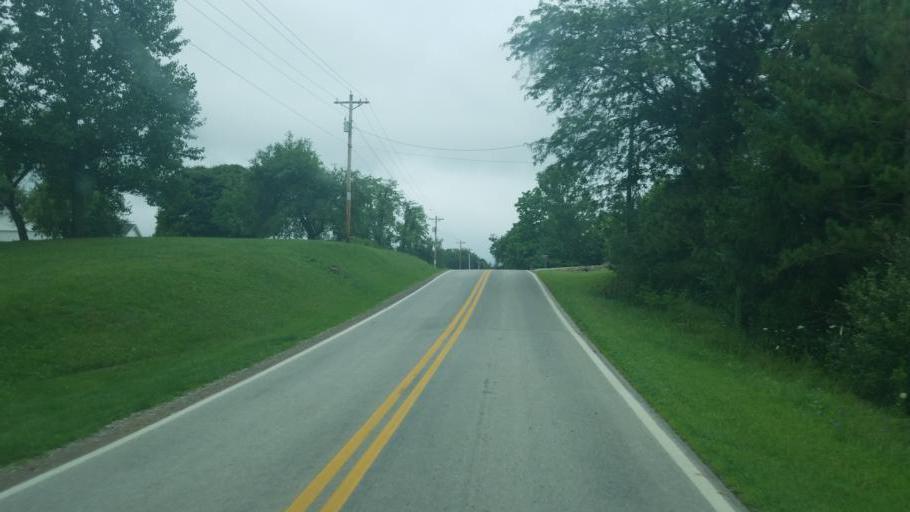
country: US
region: Ohio
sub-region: Delaware County
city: Sunbury
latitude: 40.2876
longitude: -82.8810
